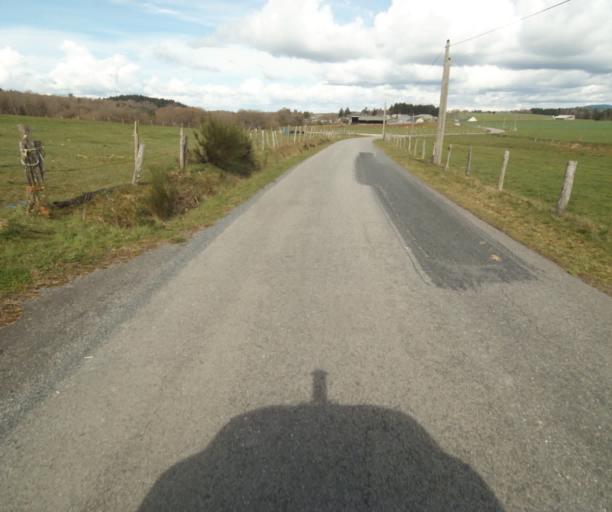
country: FR
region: Limousin
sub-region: Departement de la Correze
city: Correze
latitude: 45.3489
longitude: 1.8908
